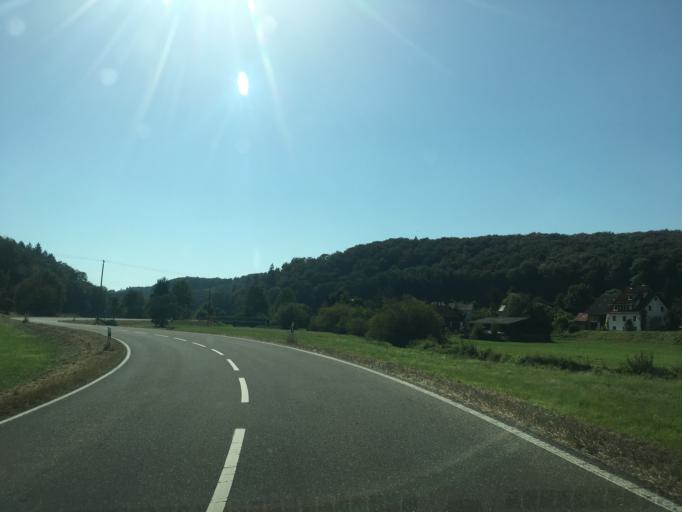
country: DE
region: Baden-Wuerttemberg
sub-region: Tuebingen Region
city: Hayingen
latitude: 48.3041
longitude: 9.4987
